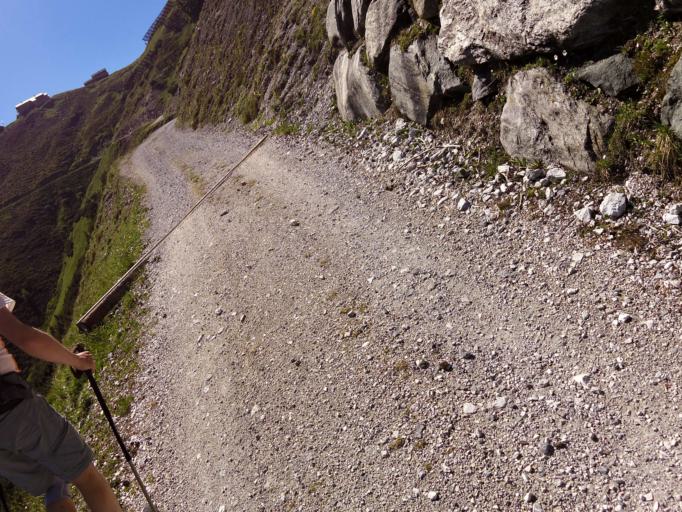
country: AT
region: Tyrol
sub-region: Politischer Bezirk Innsbruck Land
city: Neustift im Stubaital
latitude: 47.1276
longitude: 11.2854
